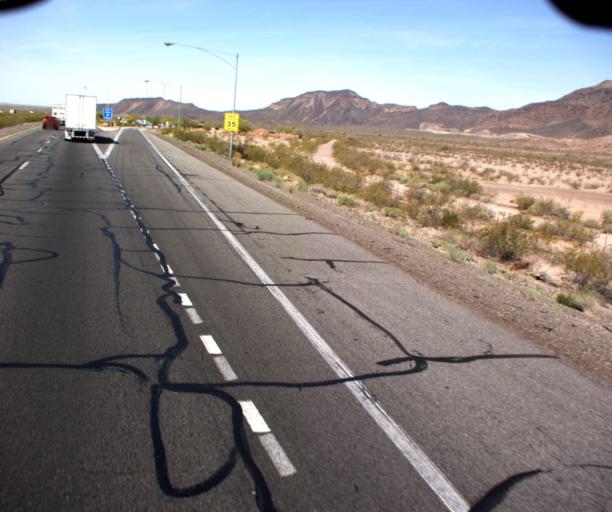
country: US
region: Arizona
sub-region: Maricopa County
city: Buckeye
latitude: 33.5197
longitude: -113.0625
